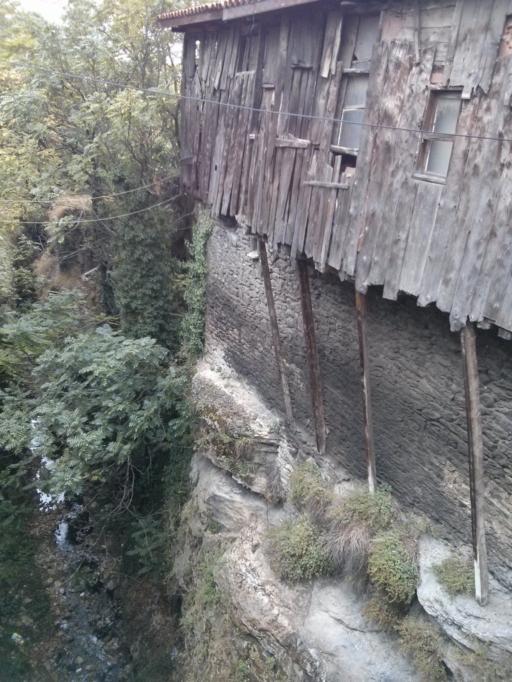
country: TR
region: Karabuk
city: Safranbolu
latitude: 41.2439
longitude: 32.6928
